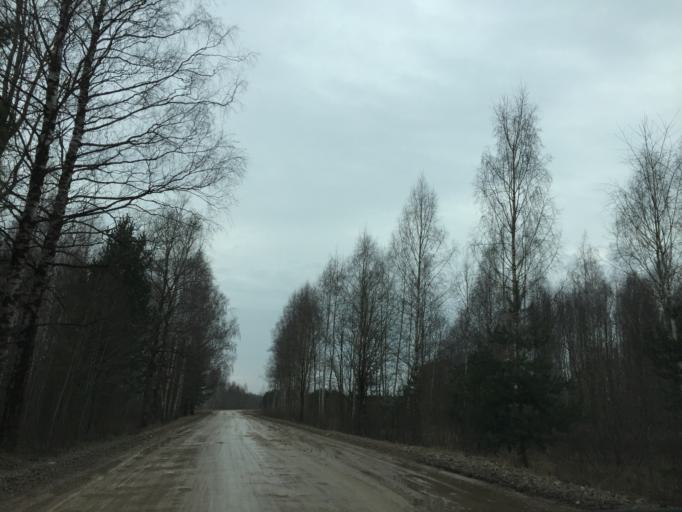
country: LV
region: Ozolnieku
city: Ozolnieki
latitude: 56.7051
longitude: 23.7578
